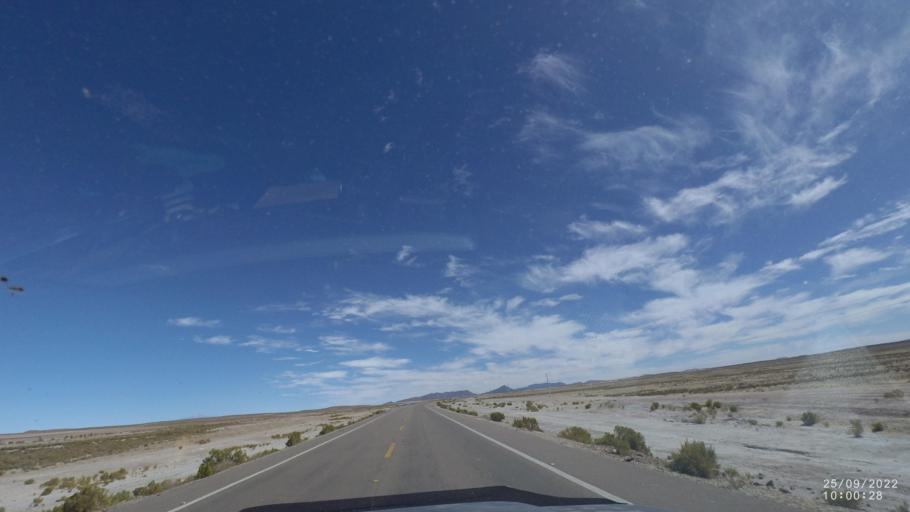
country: BO
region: Potosi
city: Colchani
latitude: -20.2733
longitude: -66.9476
